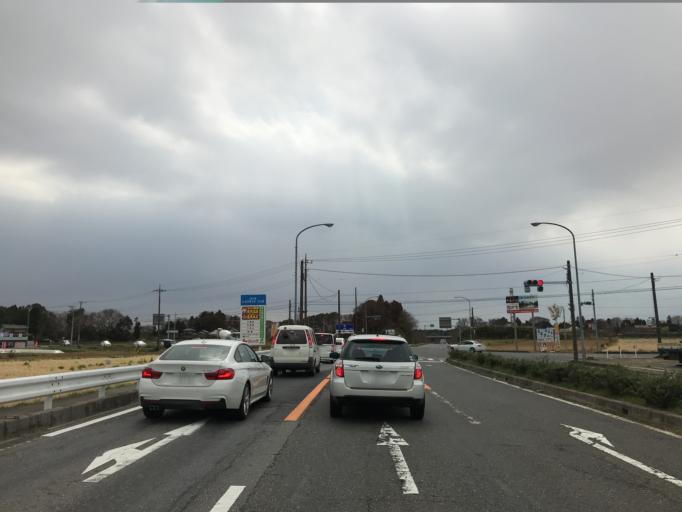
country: JP
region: Ibaraki
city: Ushiku
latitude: 36.0065
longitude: 140.0834
